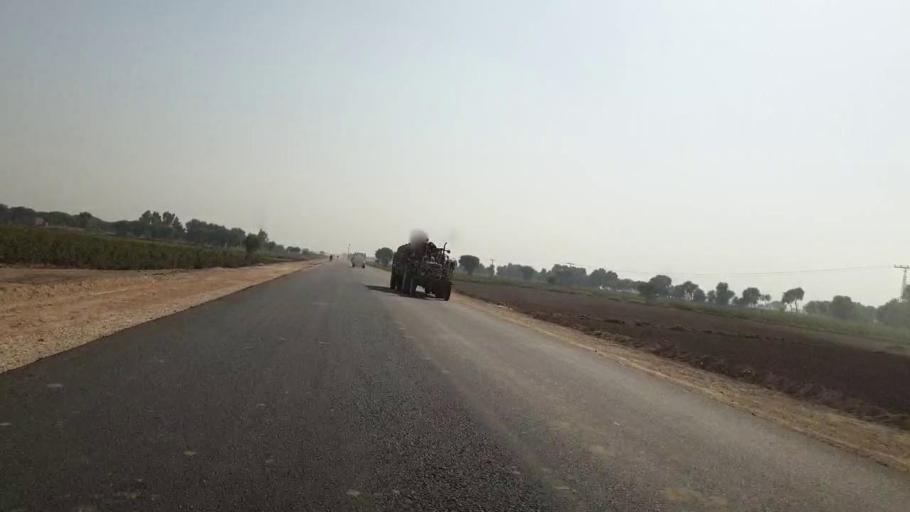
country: PK
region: Sindh
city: Dadu
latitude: 26.6647
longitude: 67.7765
